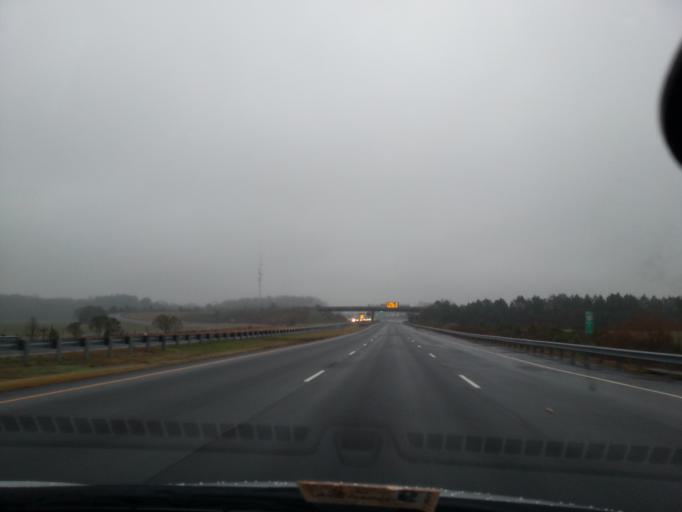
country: US
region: North Carolina
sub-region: Currituck County
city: Moyock
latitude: 36.6143
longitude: -76.2093
